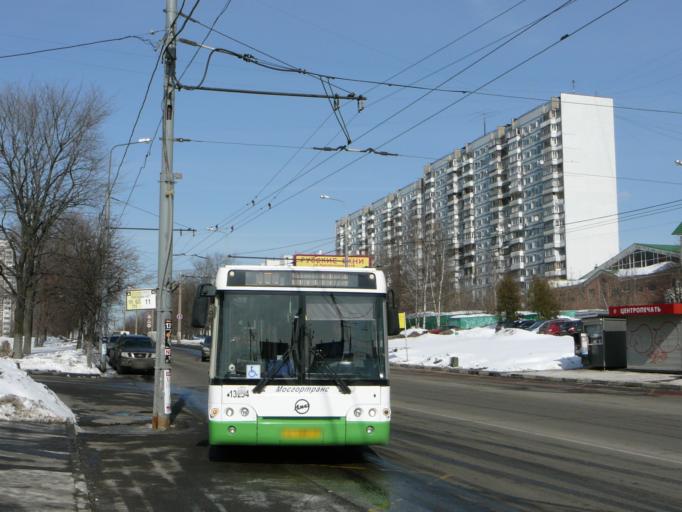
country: RU
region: Moscow
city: Orekhovo-Borisovo
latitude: 55.6145
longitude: 37.7441
